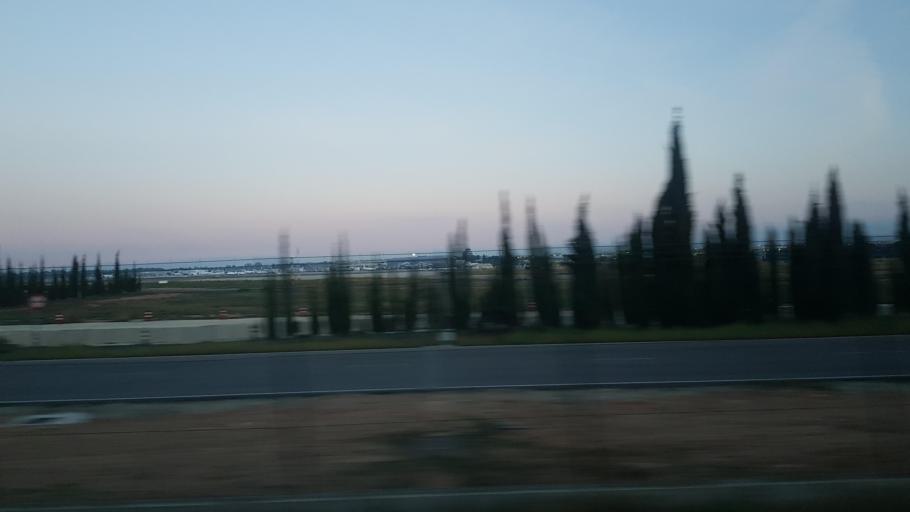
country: ES
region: Valencia
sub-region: Provincia de Valencia
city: Manises
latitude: 39.4801
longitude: -0.4674
